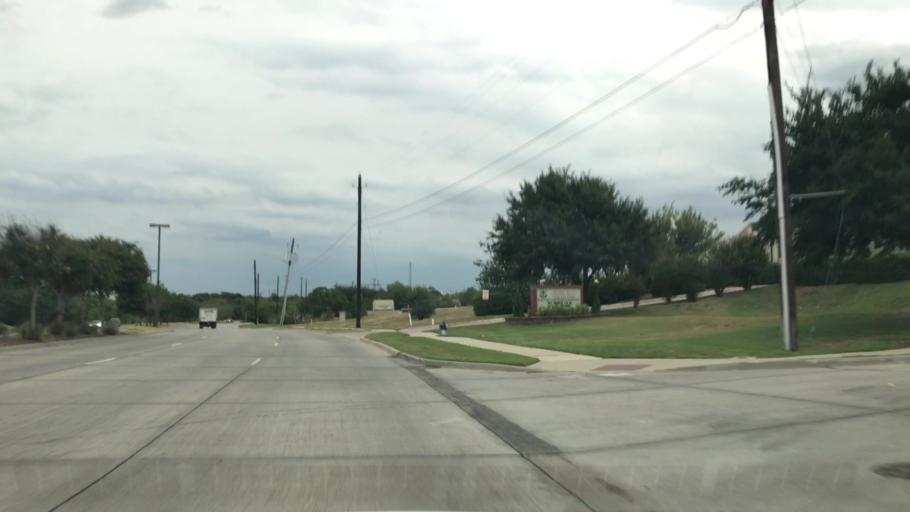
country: US
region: Texas
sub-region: Dallas County
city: Carrollton
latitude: 32.9698
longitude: -96.9115
